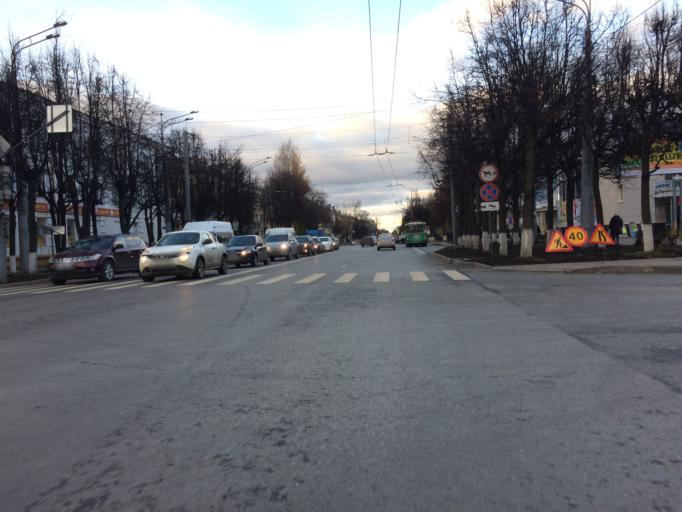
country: RU
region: Mariy-El
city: Yoshkar-Ola
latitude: 56.6346
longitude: 47.8850
